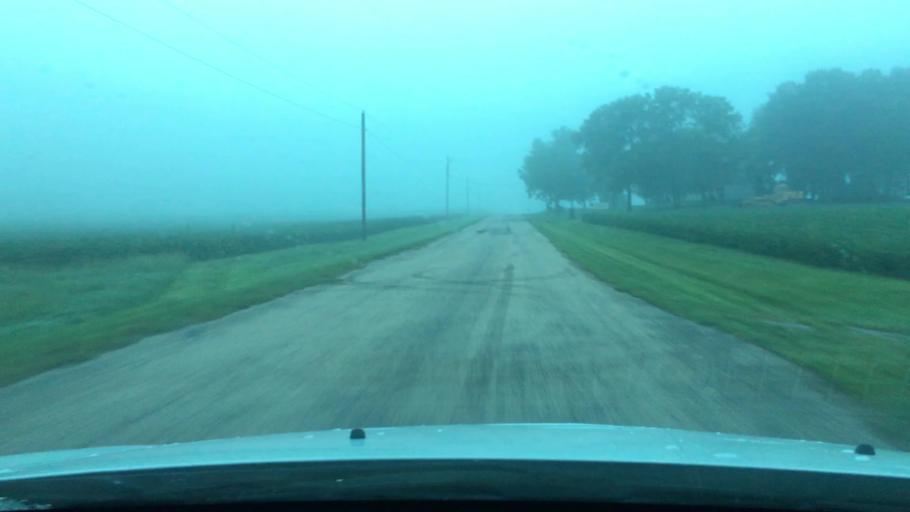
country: US
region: Illinois
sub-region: Ogle County
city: Rochelle
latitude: 41.9165
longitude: -88.9806
